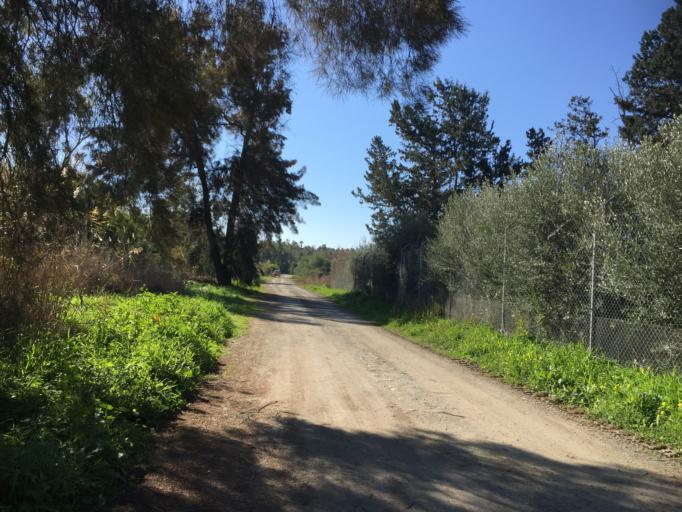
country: CY
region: Larnaka
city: Kolossi
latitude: 34.6370
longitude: 32.9683
